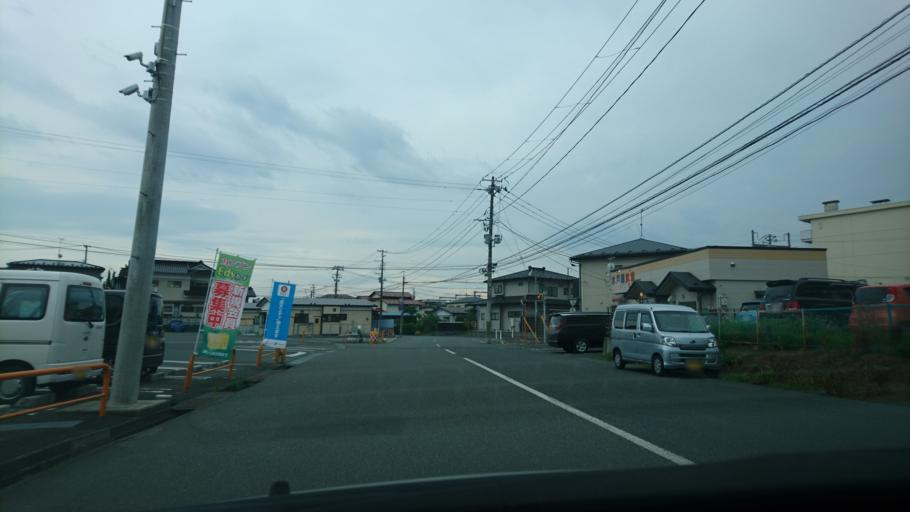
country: JP
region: Iwate
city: Ichinoseki
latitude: 38.9320
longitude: 141.1431
